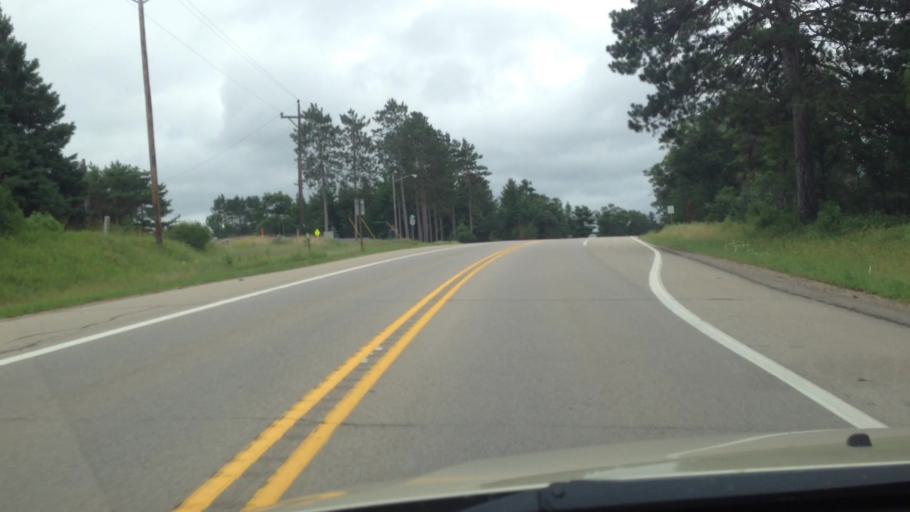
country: US
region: Michigan
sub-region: Delta County
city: Gladstone
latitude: 45.9216
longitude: -86.9357
